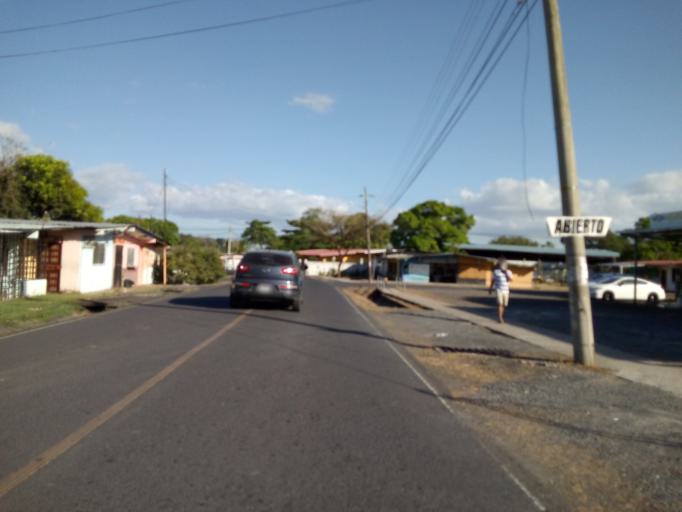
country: PA
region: Veraguas
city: Santiago de Veraguas
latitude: 8.1100
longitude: -80.9680
